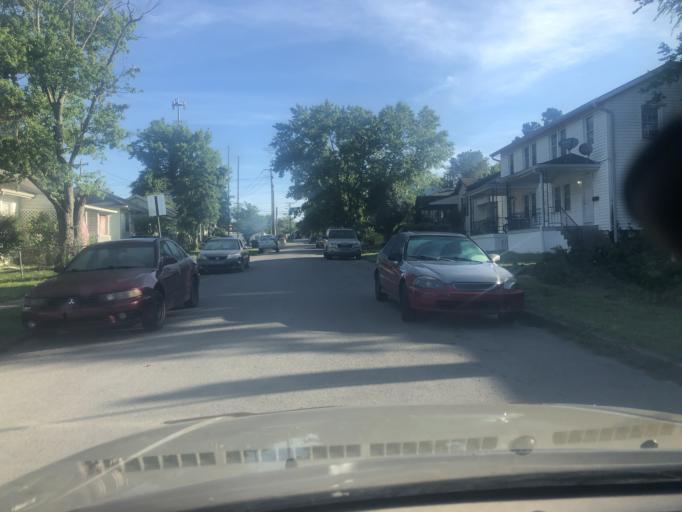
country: US
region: Tennessee
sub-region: Davidson County
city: Lakewood
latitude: 36.2566
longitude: -86.6509
